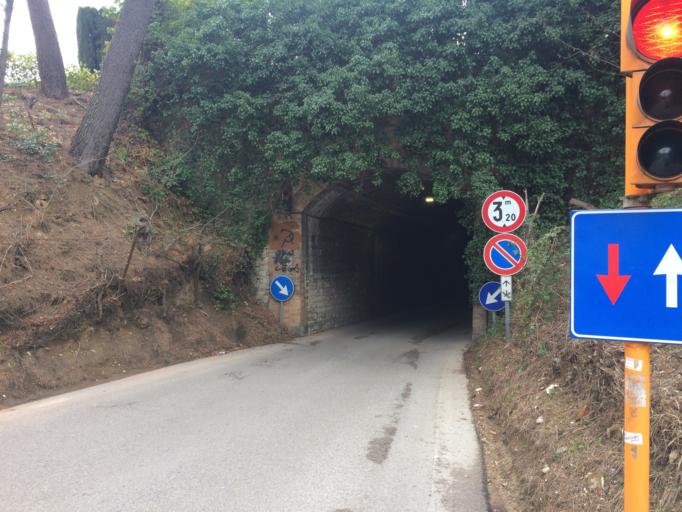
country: IT
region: Umbria
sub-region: Provincia di Perugia
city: Perugia
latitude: 43.1031
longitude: 12.3964
